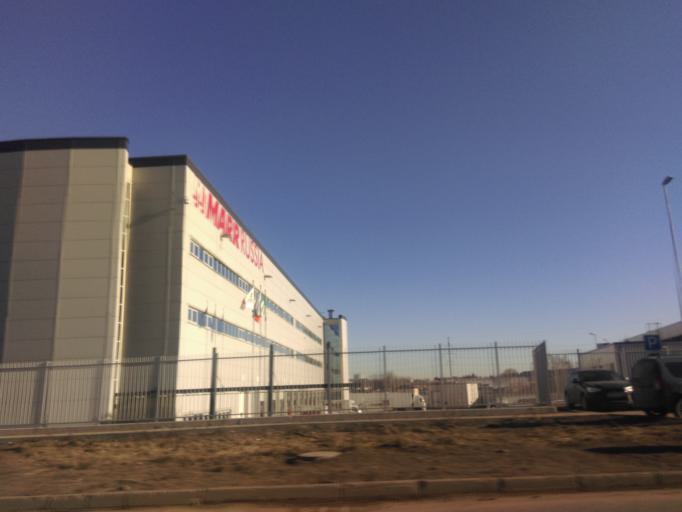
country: RU
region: Moskovskaya
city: Odintsovo
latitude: 55.6717
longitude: 37.3036
